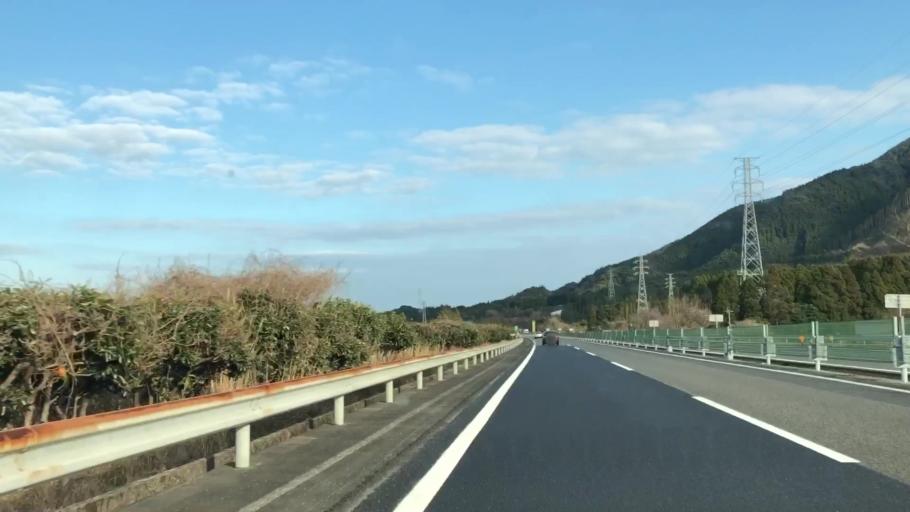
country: JP
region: Miyazaki
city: Miyazaki-shi
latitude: 31.8328
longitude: 131.3315
